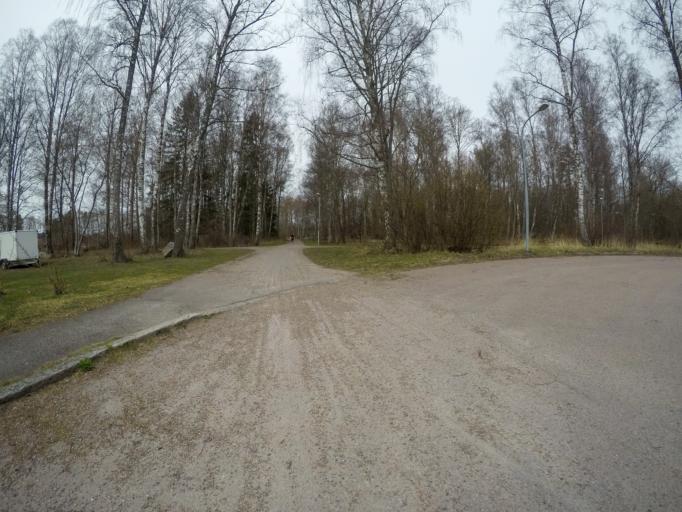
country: SE
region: Vaestmanland
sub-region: Vasteras
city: Vasteras
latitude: 59.5961
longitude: 16.6072
